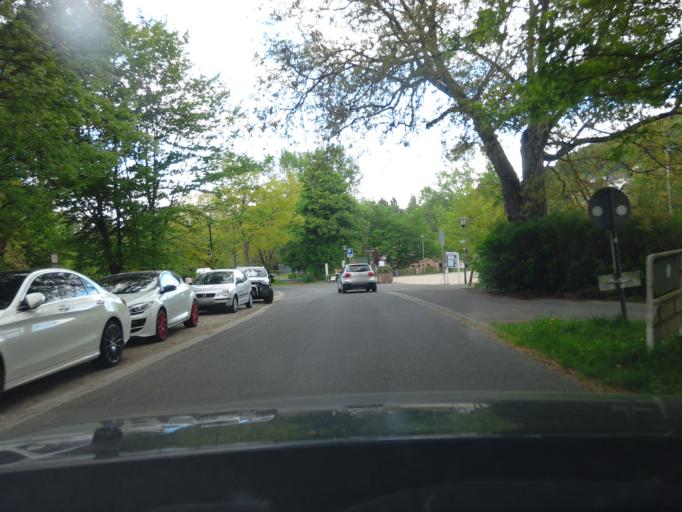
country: DE
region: Hesse
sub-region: Regierungsbezirk Darmstadt
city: Bad Orb
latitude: 50.2158
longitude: 9.3556
